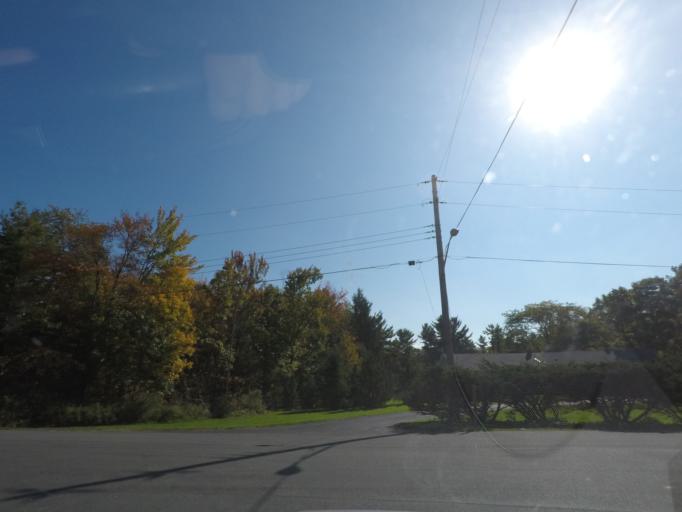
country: US
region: New York
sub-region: Rensselaer County
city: Averill Park
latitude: 42.6457
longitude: -73.5542
